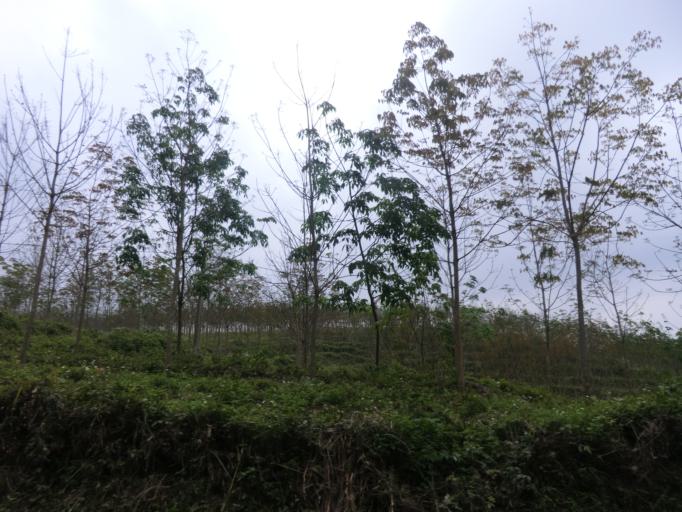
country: VN
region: Quang Binh
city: Ba Don
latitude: 17.6530
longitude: 106.4357
